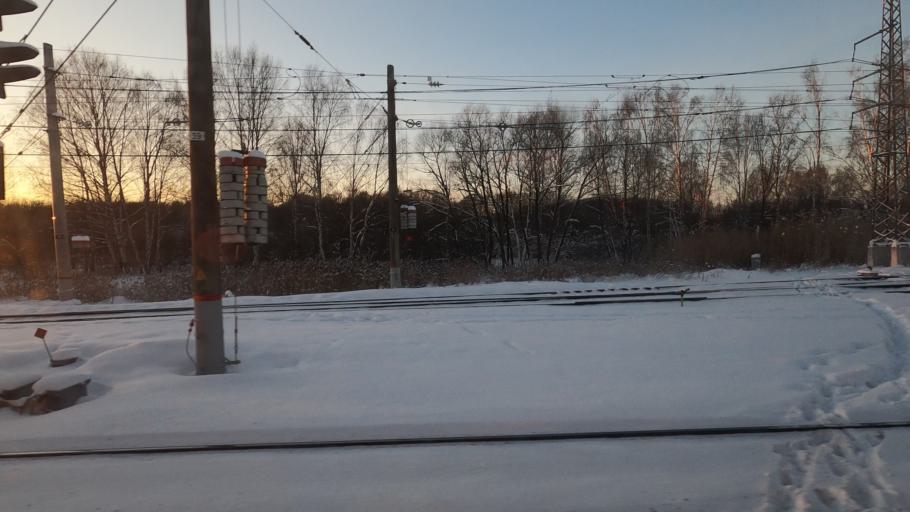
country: RU
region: Moskovskaya
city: Dmitrov
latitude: 56.3355
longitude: 37.5092
